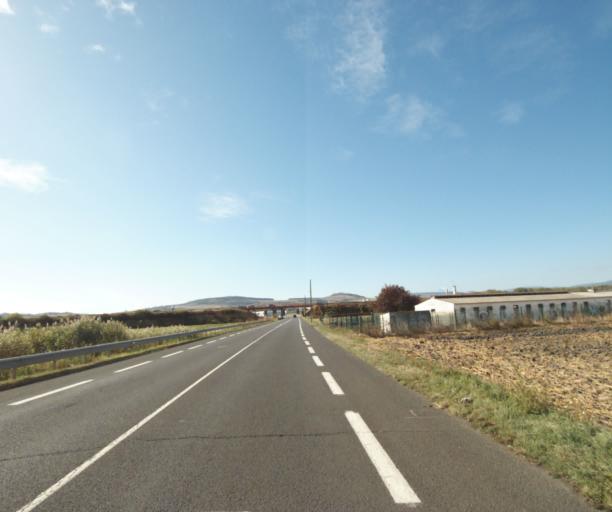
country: FR
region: Auvergne
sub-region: Departement du Puy-de-Dome
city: Malintrat
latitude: 45.7863
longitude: 3.2043
